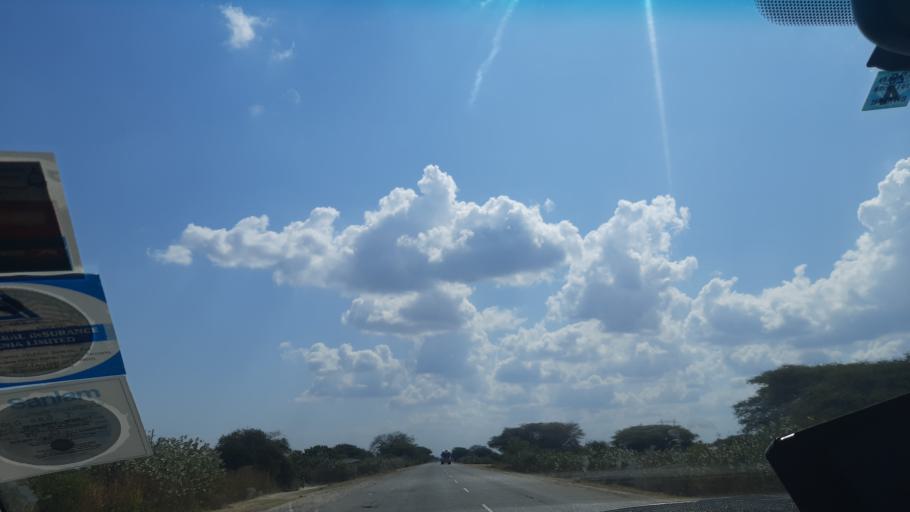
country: TZ
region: Singida
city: Kintinku
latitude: -5.9345
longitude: 35.2848
